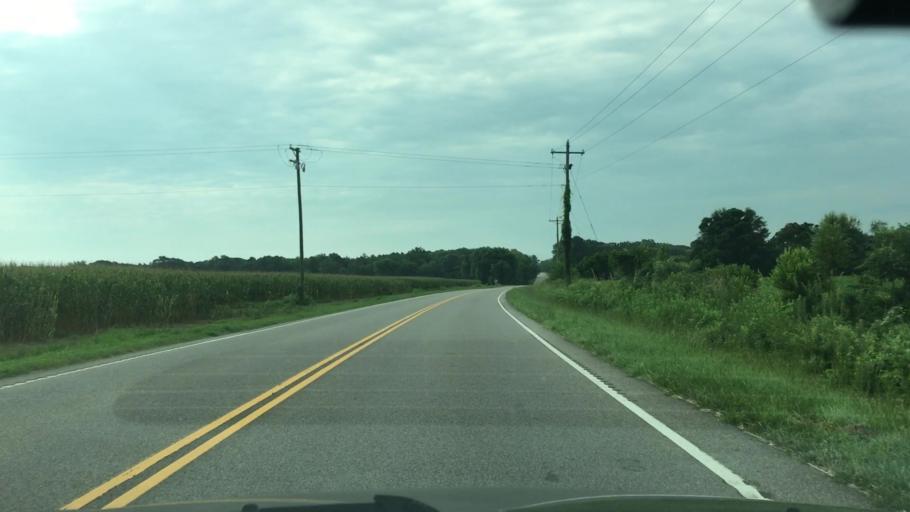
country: US
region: South Carolina
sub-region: Lexington County
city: Batesburg-Leesville
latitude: 33.6981
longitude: -81.4777
